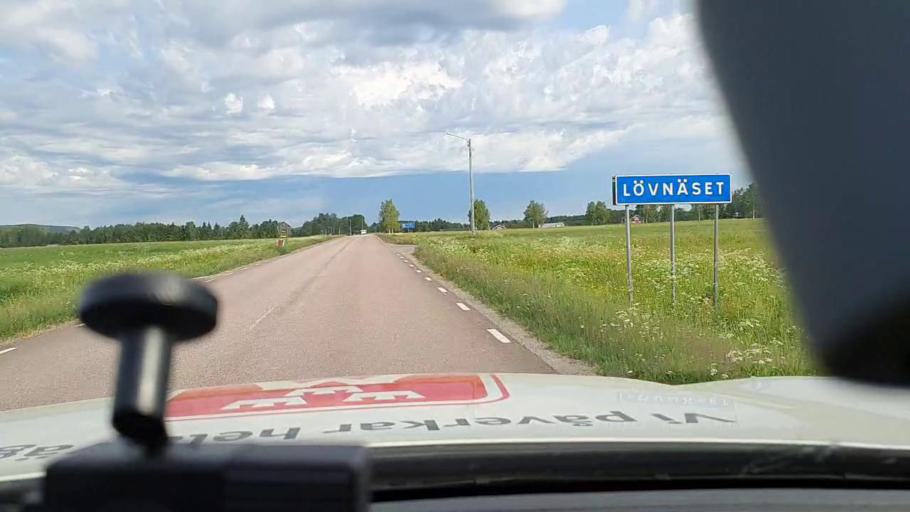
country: SE
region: Norrbotten
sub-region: Bodens Kommun
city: Saevast
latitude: 65.6926
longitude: 21.7825
